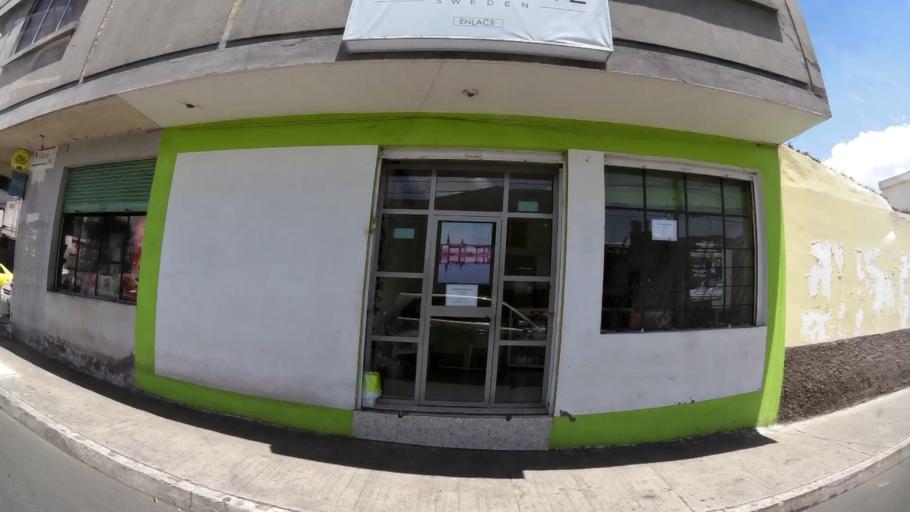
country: EC
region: Chimborazo
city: Riobamba
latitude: -1.6724
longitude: -78.6436
